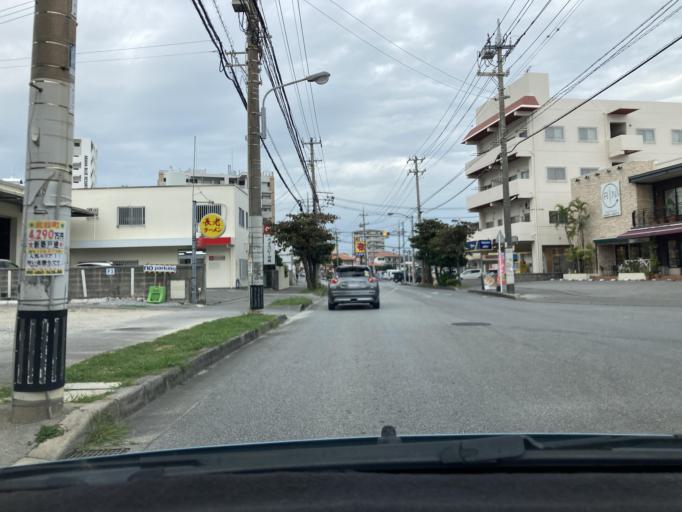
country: JP
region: Okinawa
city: Chatan
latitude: 26.3080
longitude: 127.7615
